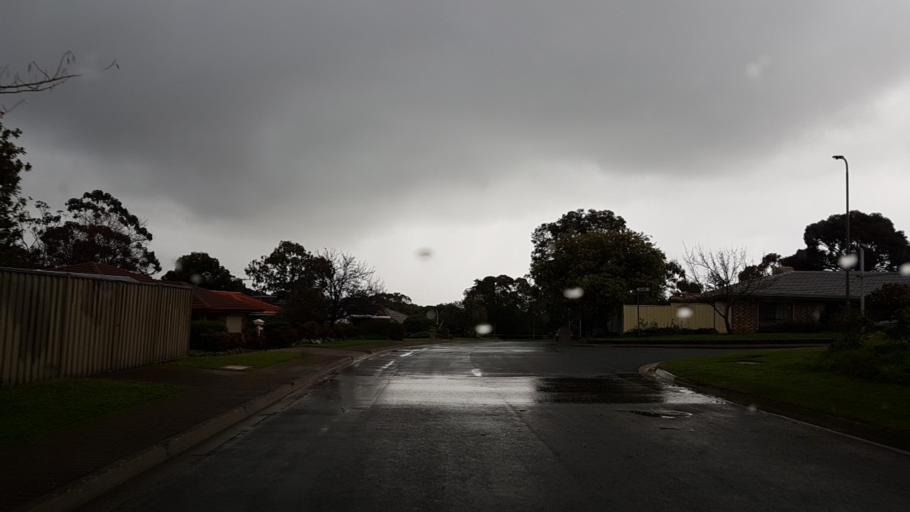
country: AU
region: South Australia
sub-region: Onkaparinga
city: Craigburn Farm
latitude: -35.0855
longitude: 138.5882
